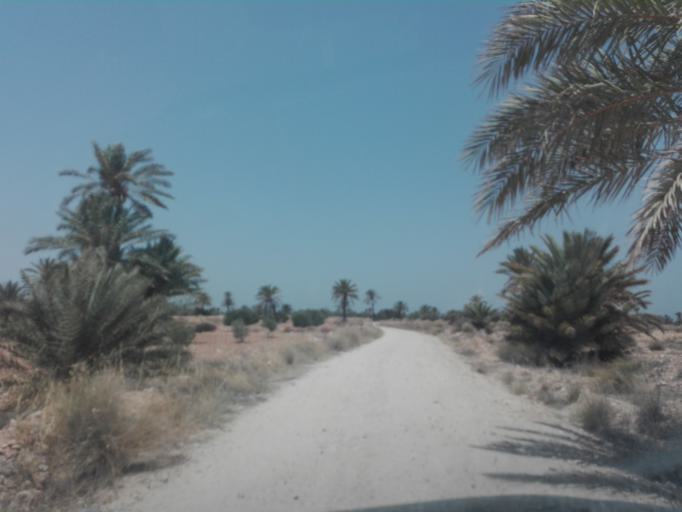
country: TN
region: Safaqis
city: Al Qarmadah
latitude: 34.6592
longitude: 11.1004
